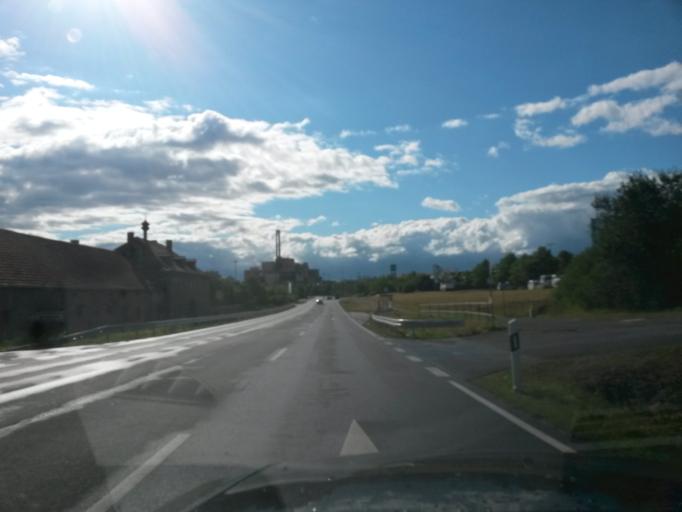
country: DE
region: Bavaria
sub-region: Regierungsbezirk Unterfranken
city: Gerbrunn
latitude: 49.7915
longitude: 10.0046
